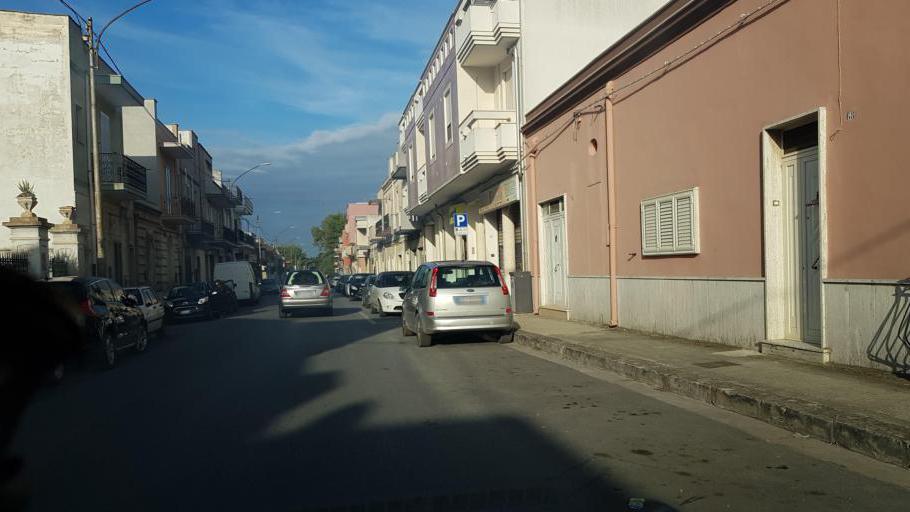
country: IT
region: Apulia
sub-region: Provincia di Brindisi
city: Francavilla Fontana
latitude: 40.5337
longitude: 17.5869
